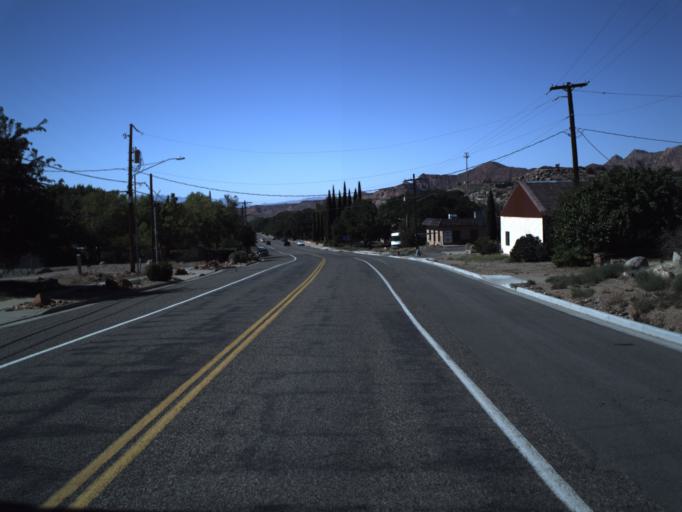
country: US
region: Utah
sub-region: Washington County
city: Toquerville
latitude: 37.2401
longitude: -113.3571
